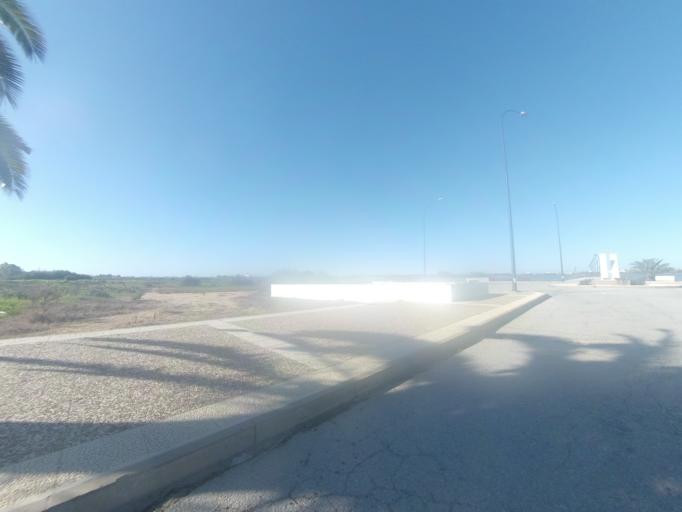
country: ES
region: Andalusia
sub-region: Provincia de Huelva
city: Palos de la Frontera
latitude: 37.2305
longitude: -6.9069
